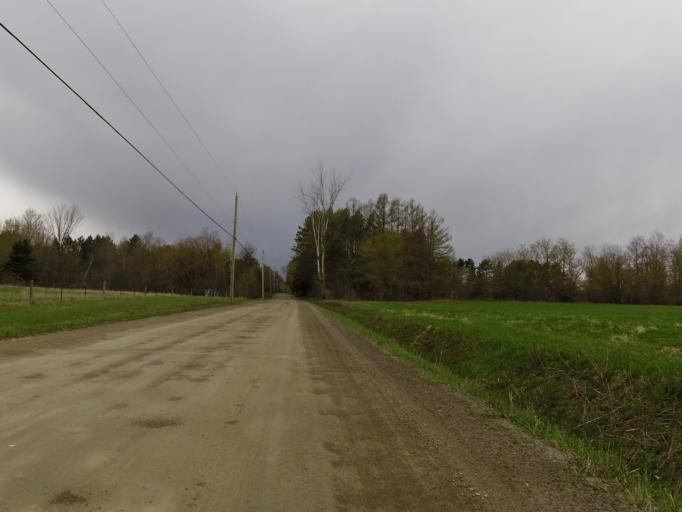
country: CA
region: Ontario
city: Hawkesbury
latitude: 45.6195
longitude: -74.5421
